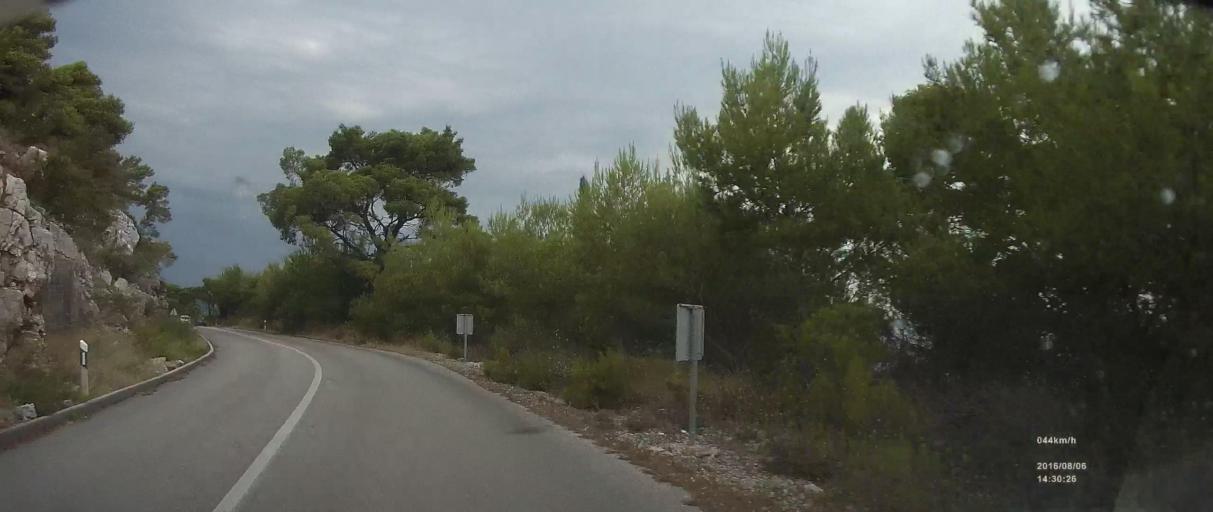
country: HR
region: Dubrovacko-Neretvanska
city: Ston
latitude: 42.7107
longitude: 17.7283
